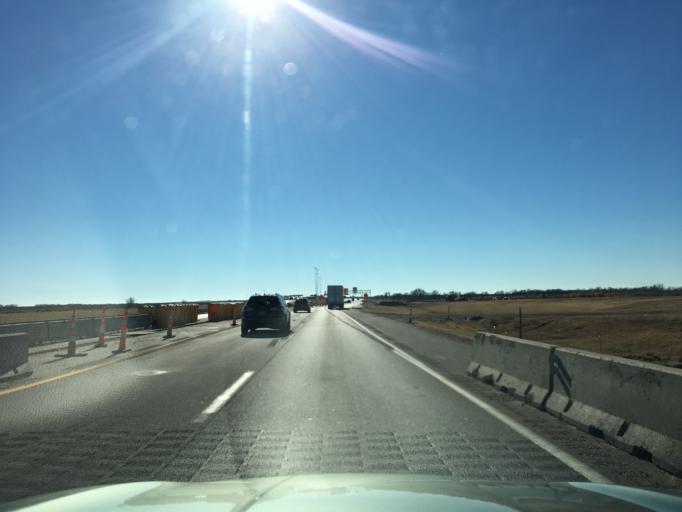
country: US
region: Kansas
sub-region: Sumner County
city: Wellington
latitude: 37.2469
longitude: -97.3390
